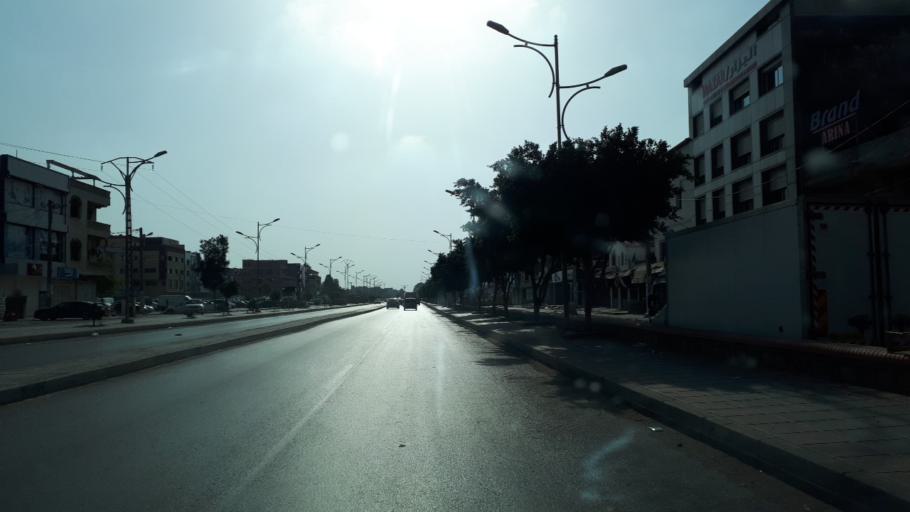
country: DZ
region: Alger
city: Dar el Beida
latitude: 36.7305
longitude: 3.2349
